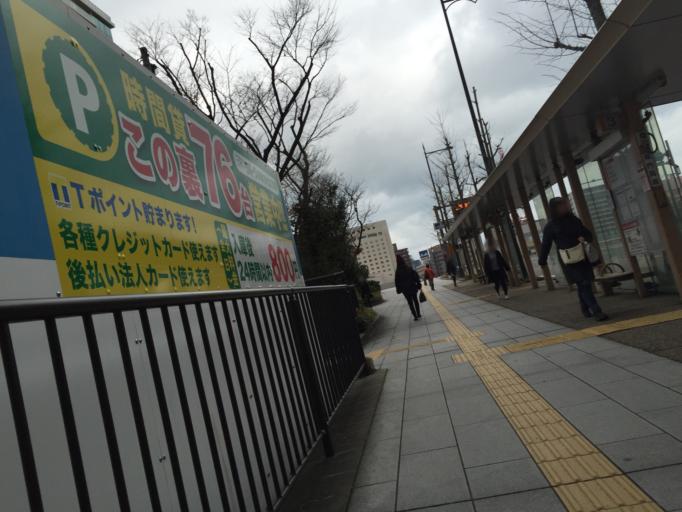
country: JP
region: Niigata
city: Niigata-shi
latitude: 37.9184
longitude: 139.0555
